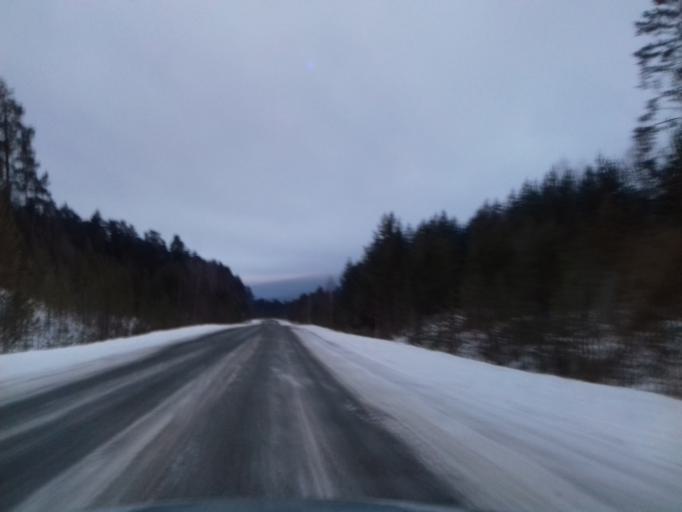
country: RU
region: Bashkortostan
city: Verkhniy Avzyan
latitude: 53.7424
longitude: 57.9137
